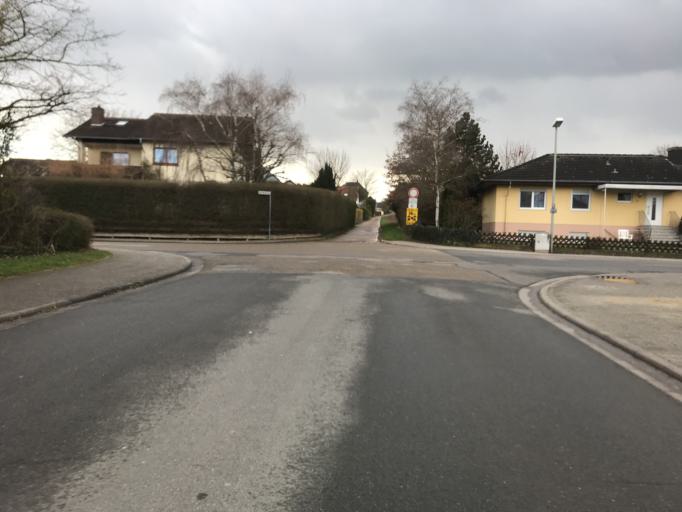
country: DE
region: Rheinland-Pfalz
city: Ober-Saulheim
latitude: 49.8749
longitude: 8.1448
